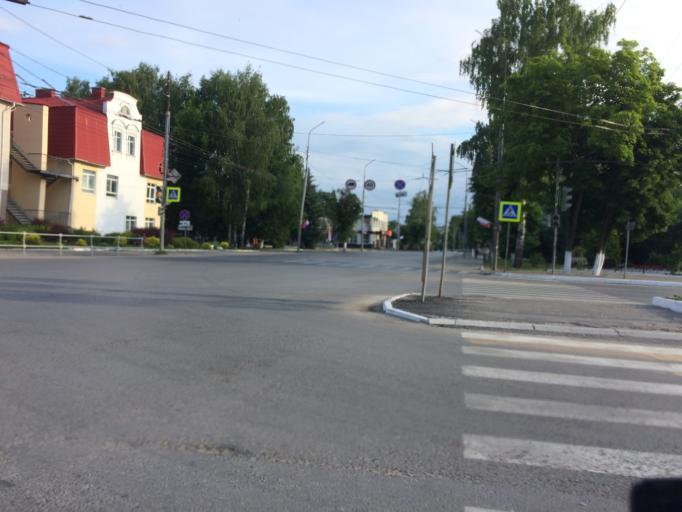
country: RU
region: Mariy-El
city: Medvedevo
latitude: 56.6325
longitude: 47.8041
